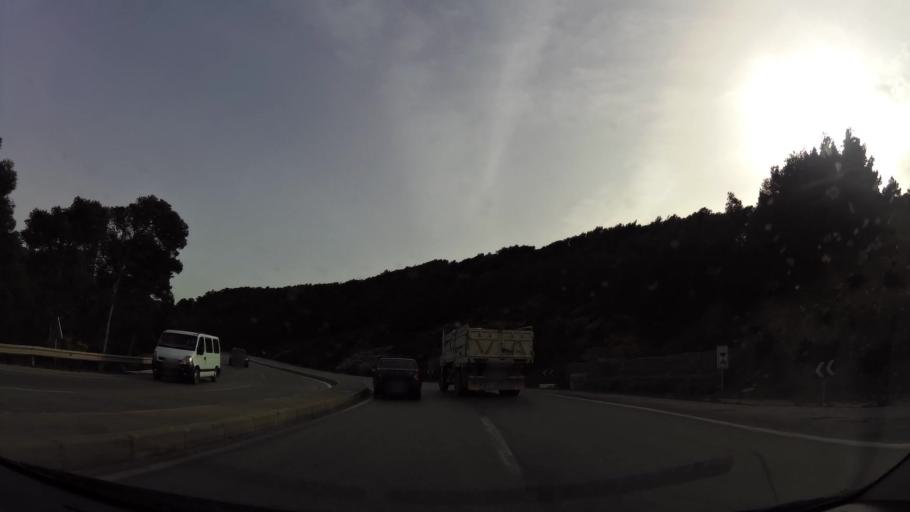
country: MA
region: Tanger-Tetouan
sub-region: Tanger-Assilah
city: Dar Chaoui
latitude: 35.5636
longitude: -5.5852
